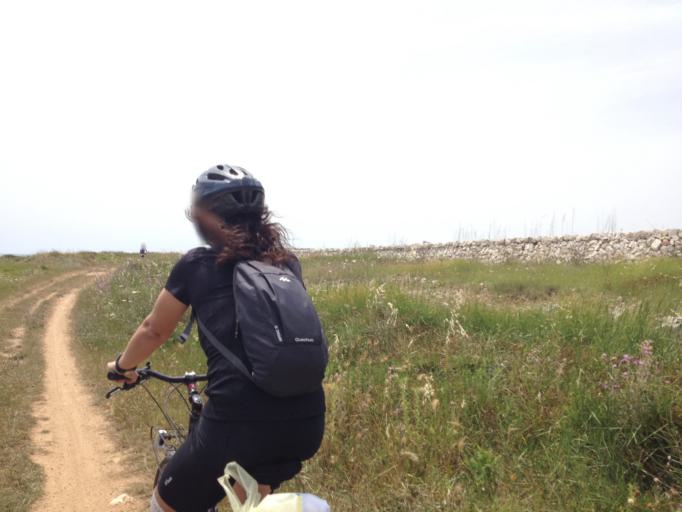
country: IT
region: Apulia
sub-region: Provincia di Lecce
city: Borgagne
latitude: 40.2623
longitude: 18.4430
